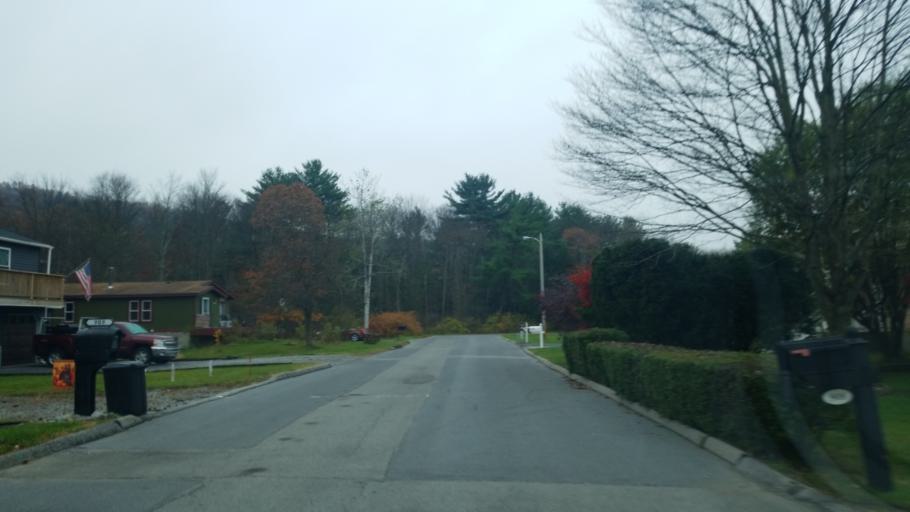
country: US
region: Pennsylvania
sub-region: Clearfield County
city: Clearfield
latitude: 41.0061
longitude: -78.4394
